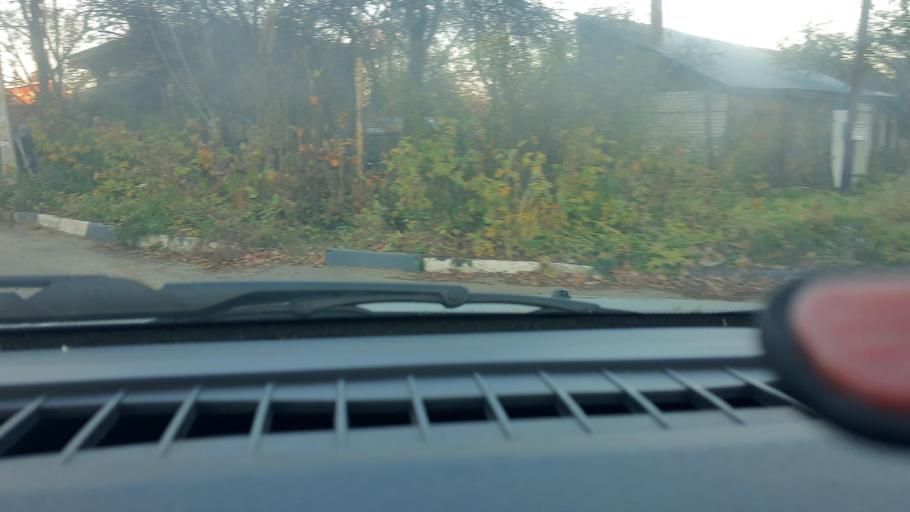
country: RU
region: Nizjnij Novgorod
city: Nizhniy Novgorod
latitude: 56.2740
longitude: 44.0012
